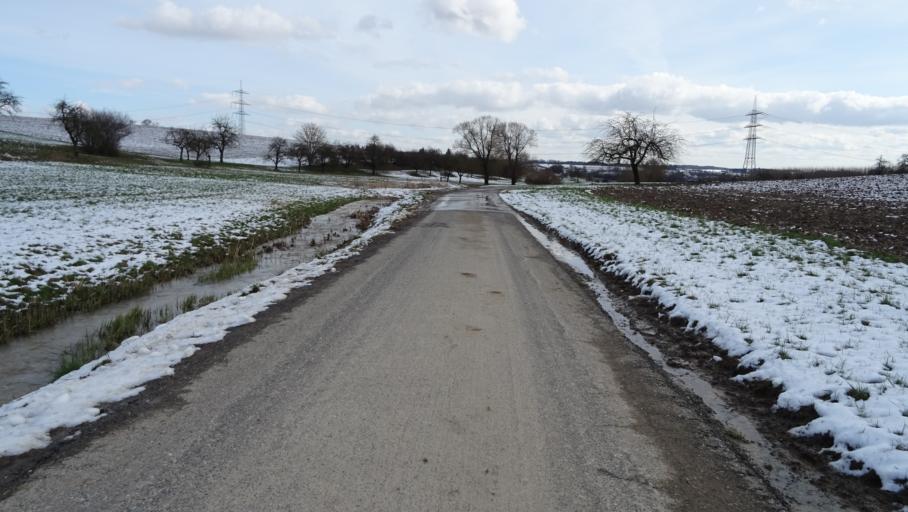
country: DE
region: Baden-Wuerttemberg
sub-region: Karlsruhe Region
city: Seckach
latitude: 49.4249
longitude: 9.2693
